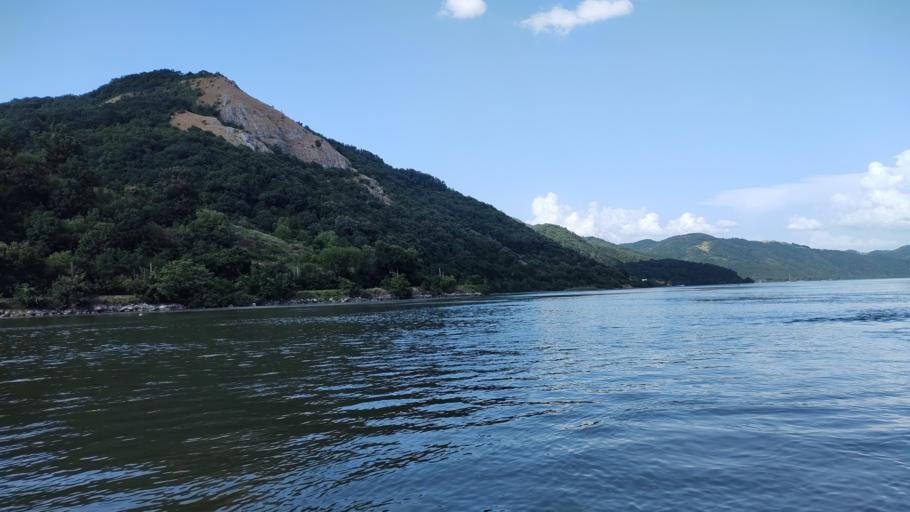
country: RO
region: Caras-Severin
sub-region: Comuna Pescari
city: Coronini
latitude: 44.6552
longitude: 21.7391
